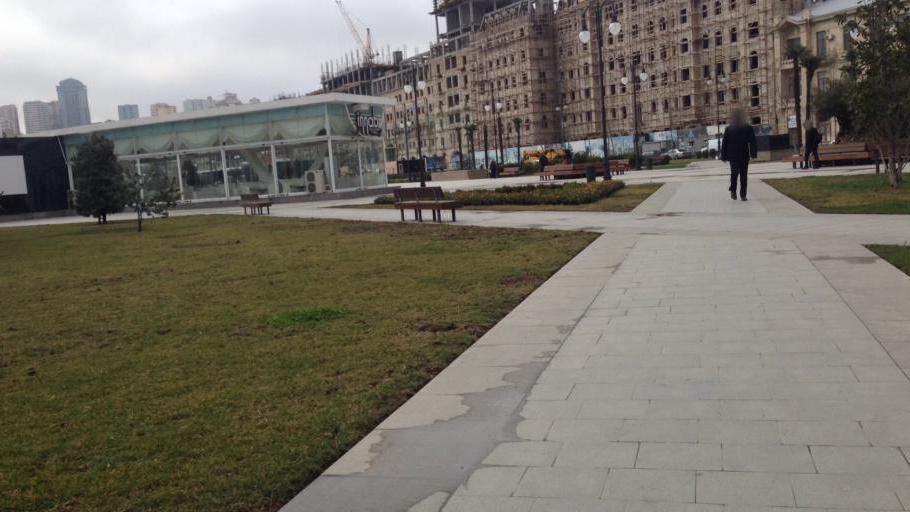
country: AZ
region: Baki
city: Badamdar
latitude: 40.3766
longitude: 49.8381
